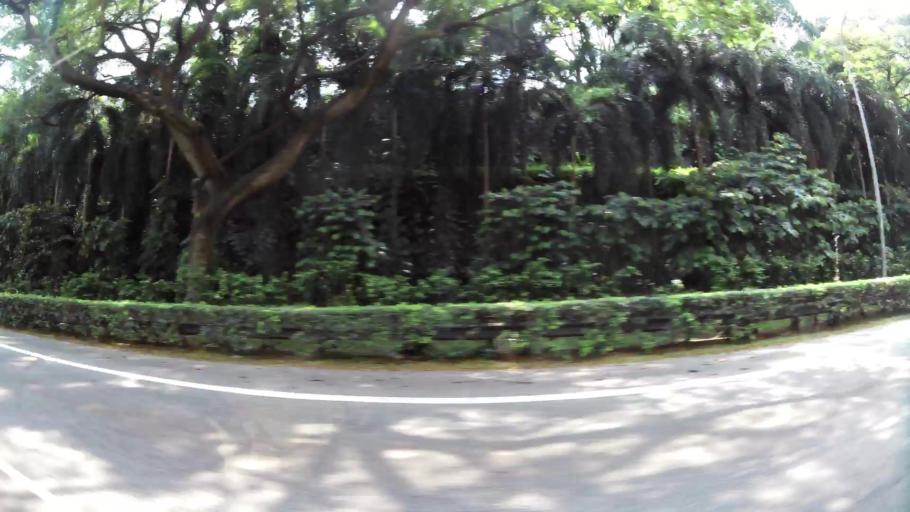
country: SG
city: Singapore
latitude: 1.2798
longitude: 103.8184
